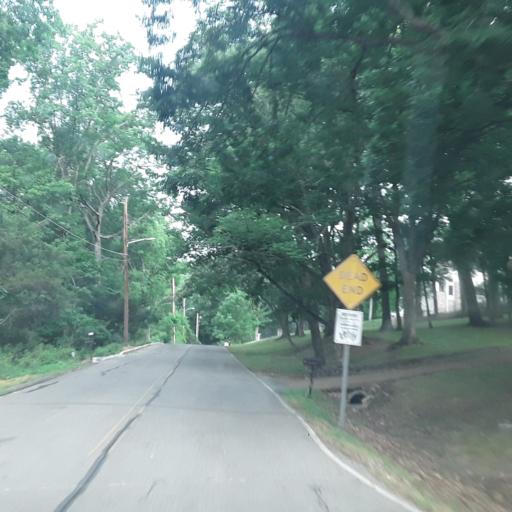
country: US
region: Tennessee
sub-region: Williamson County
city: Brentwood
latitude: 36.0566
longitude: -86.7787
